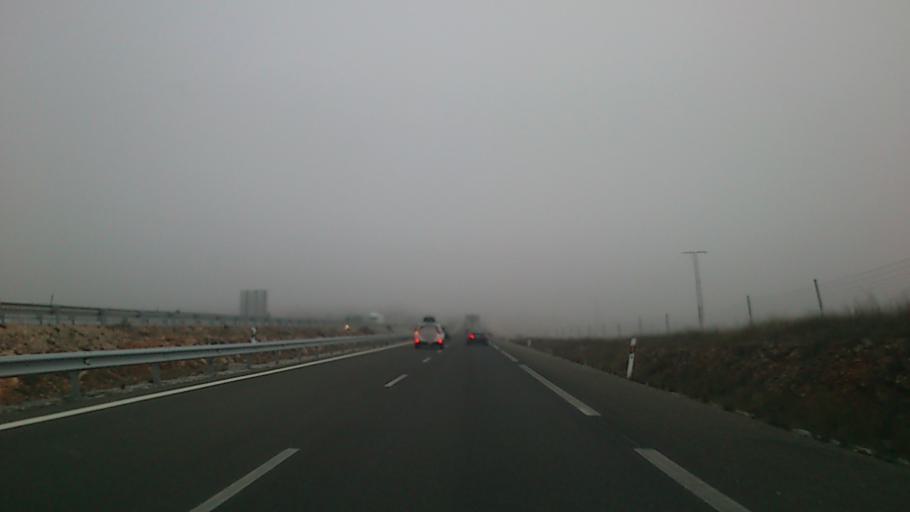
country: ES
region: Castille-La Mancha
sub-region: Provincia de Guadalajara
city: Algora
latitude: 40.9608
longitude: -2.6548
